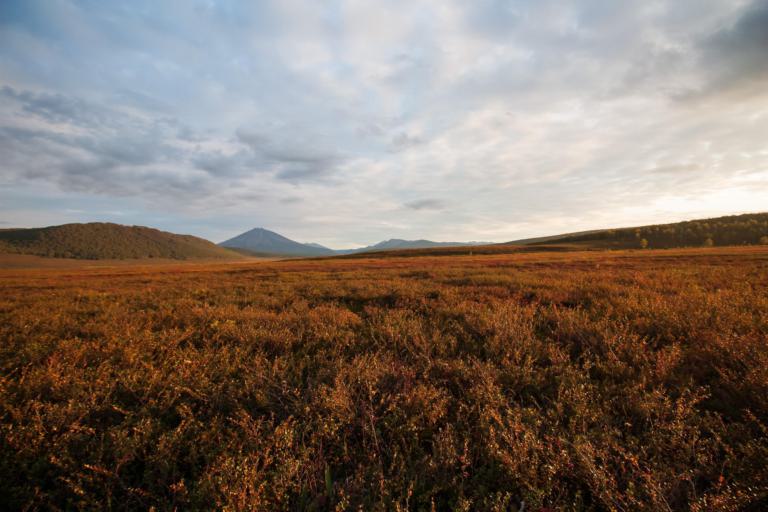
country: RU
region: Kamtsjatka
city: Yelizovo
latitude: 53.7433
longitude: 158.6686
